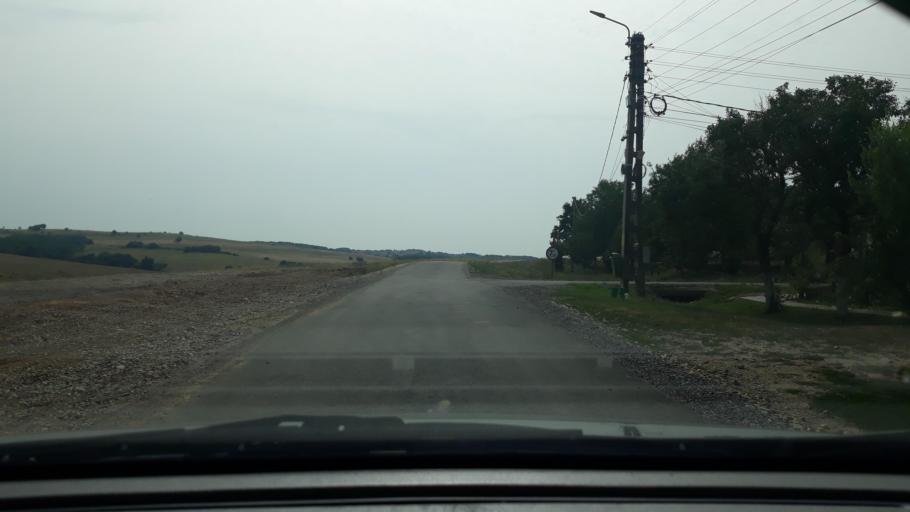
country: RO
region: Bihor
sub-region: Comuna Tauteu
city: Tauteu
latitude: 47.2662
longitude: 22.3271
